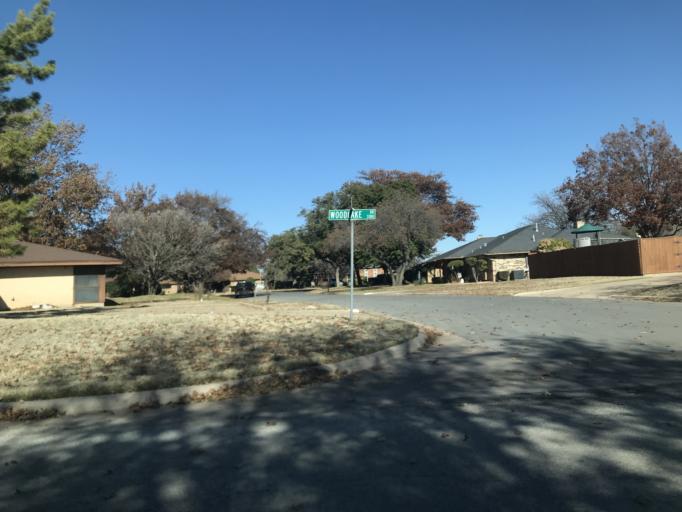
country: US
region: Texas
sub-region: Taylor County
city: Abilene
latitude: 32.3828
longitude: -99.7648
